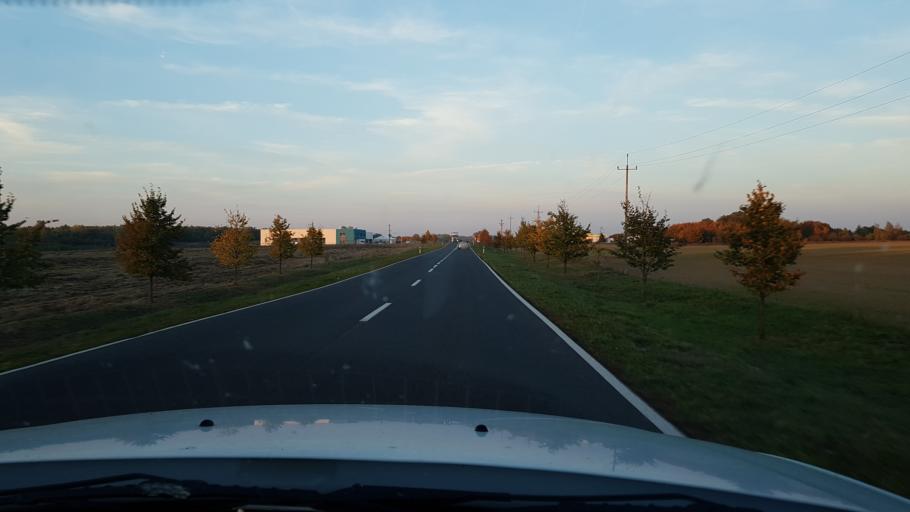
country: PL
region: West Pomeranian Voivodeship
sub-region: Powiat policki
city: Kolbaskowo
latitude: 53.3197
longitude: 14.4174
